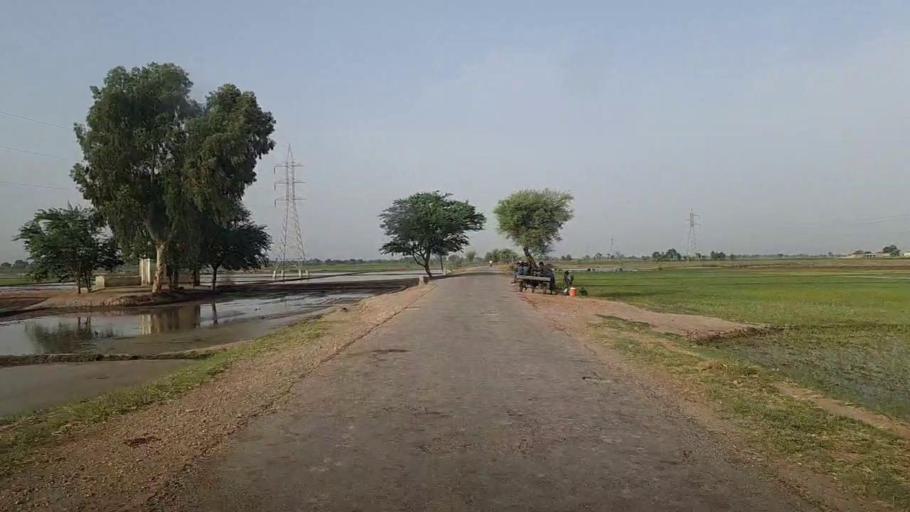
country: PK
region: Sindh
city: Mehar
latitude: 27.1425
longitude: 67.7948
